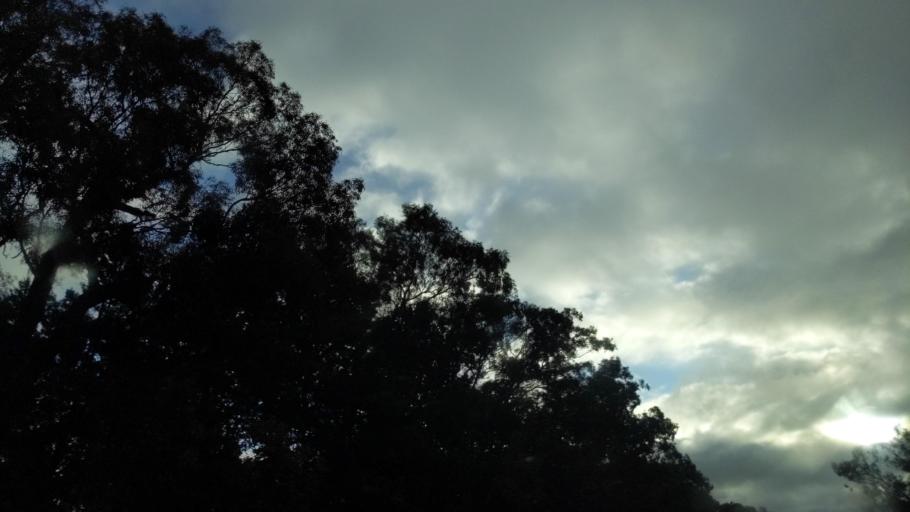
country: AU
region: New South Wales
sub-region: Coolamon
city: Coolamon
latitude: -34.8645
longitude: 147.2424
